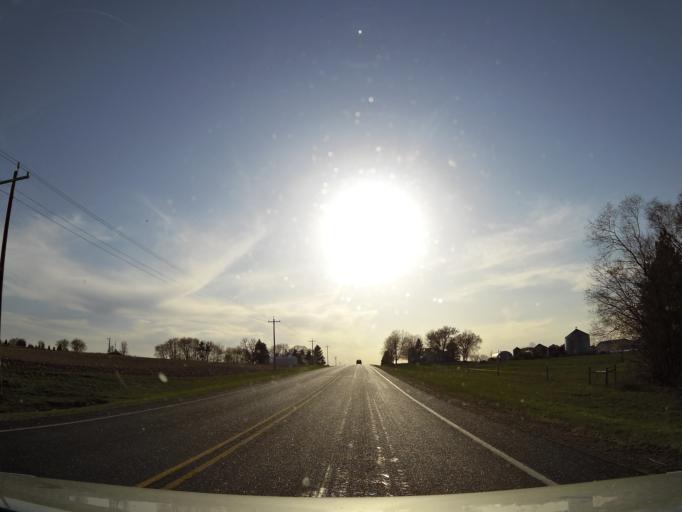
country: US
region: Wisconsin
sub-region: Pierce County
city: River Falls
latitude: 44.8244
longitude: -92.7082
